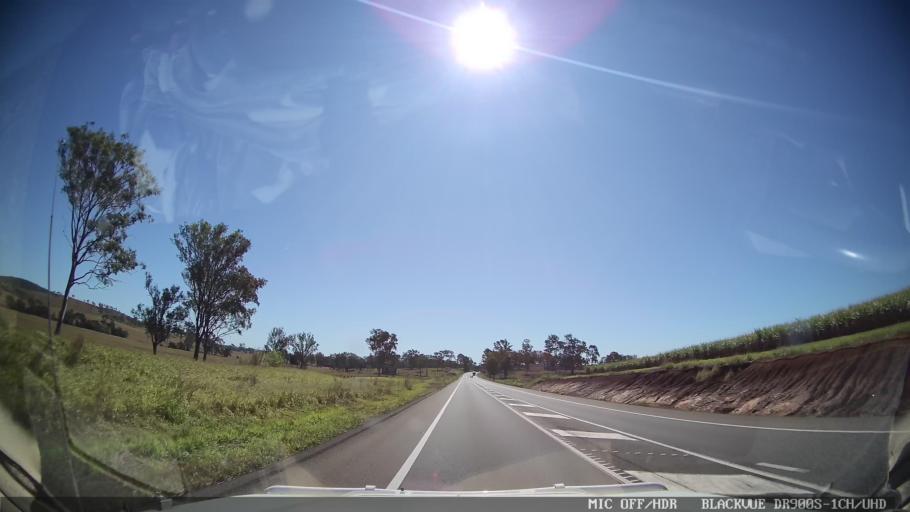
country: AU
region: Queensland
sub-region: Fraser Coast
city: Maryborough
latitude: -25.7783
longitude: 152.5962
